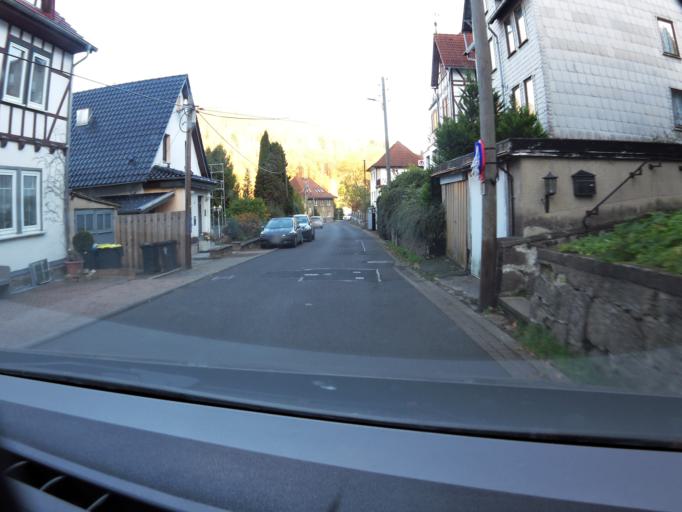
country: DE
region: Thuringia
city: Ruhla
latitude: 50.8899
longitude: 10.3645
